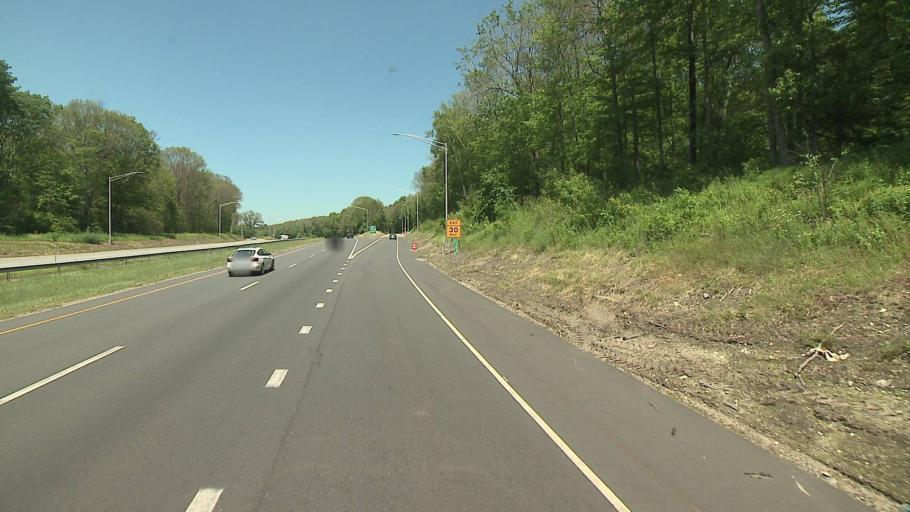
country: US
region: Connecticut
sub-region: Windham County
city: Danielson
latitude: 41.7988
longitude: -71.8740
